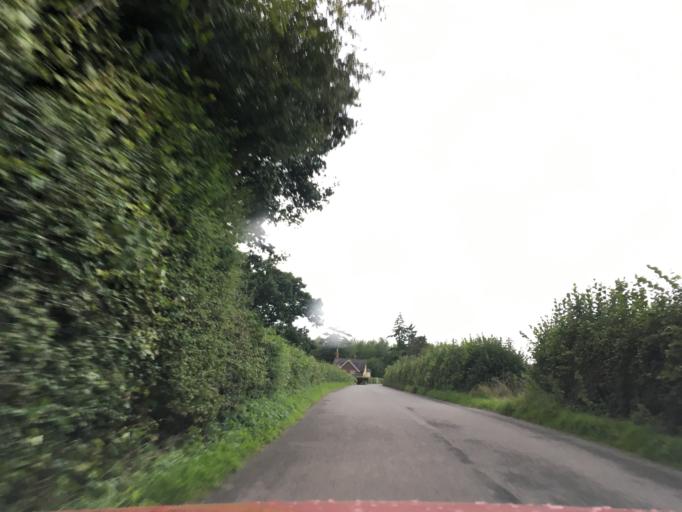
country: GB
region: Wales
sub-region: Monmouthshire
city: Llangybi
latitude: 51.6688
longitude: -2.8703
